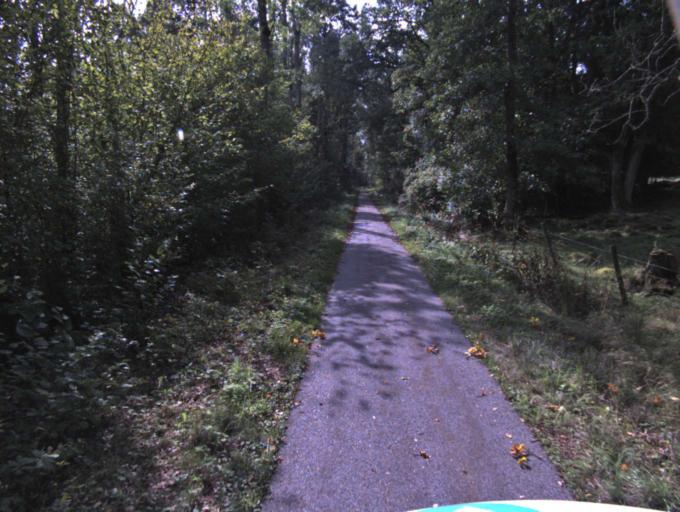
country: SE
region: Vaestra Goetaland
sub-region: Tranemo Kommun
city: Limmared
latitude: 57.6476
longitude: 13.3602
